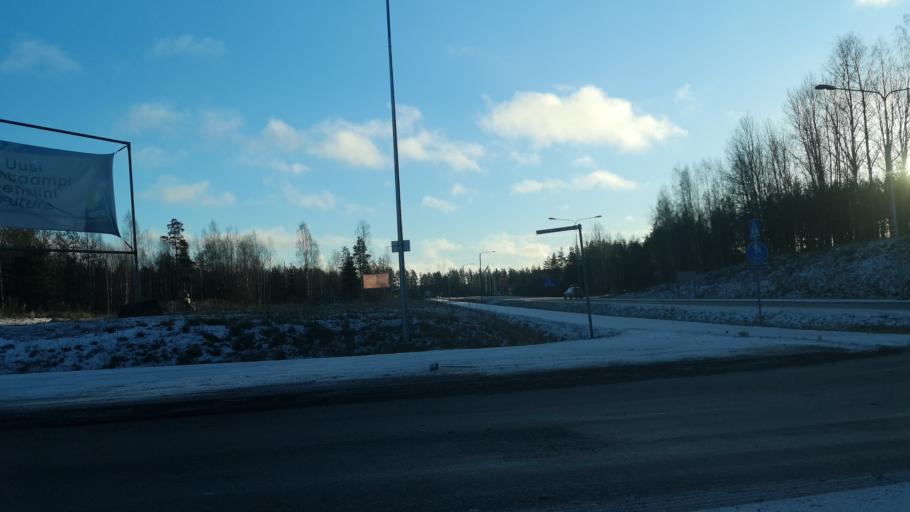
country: FI
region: Paijanne Tavastia
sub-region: Lahti
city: Heinola
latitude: 61.1117
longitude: 25.9290
